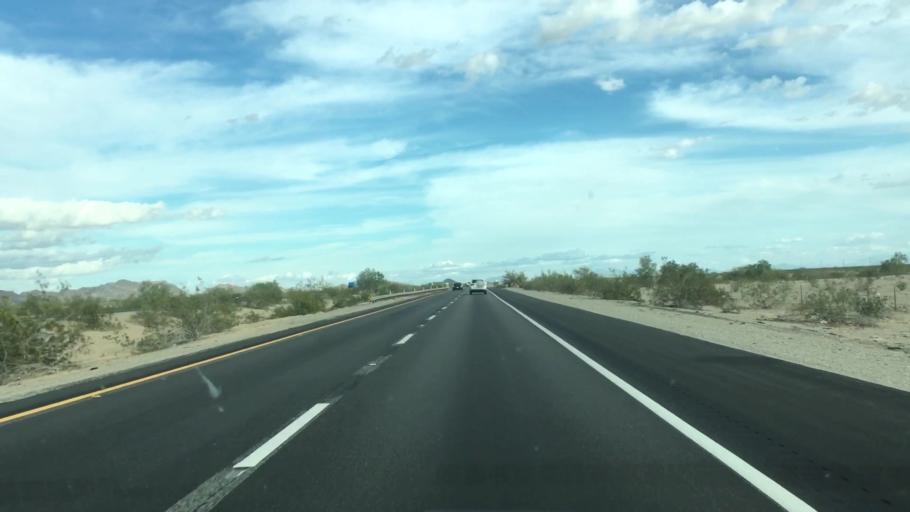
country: US
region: California
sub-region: Riverside County
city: Mesa Verde
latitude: 33.6094
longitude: -114.8478
